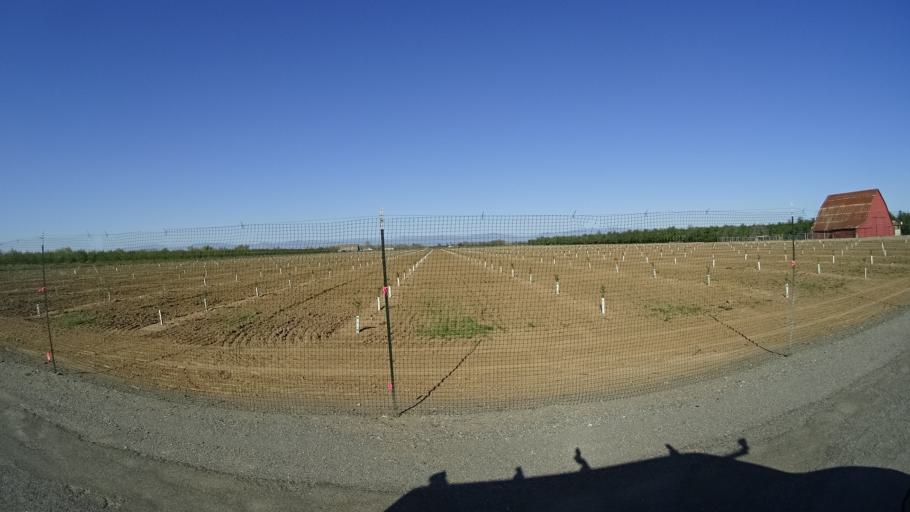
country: US
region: California
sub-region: Glenn County
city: Orland
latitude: 39.7661
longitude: -122.1321
